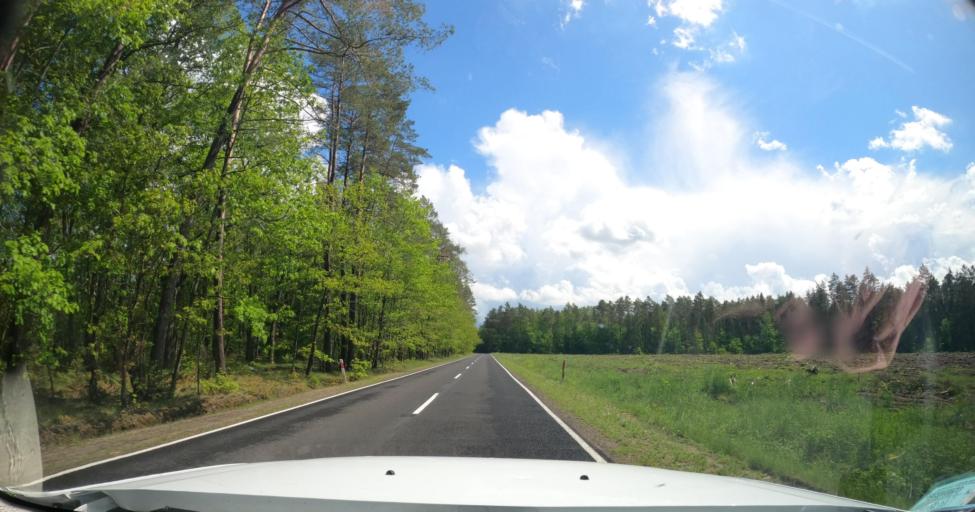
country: PL
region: Pomeranian Voivodeship
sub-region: Powiat bytowski
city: Czarna Dabrowka
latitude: 54.3861
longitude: 17.4807
